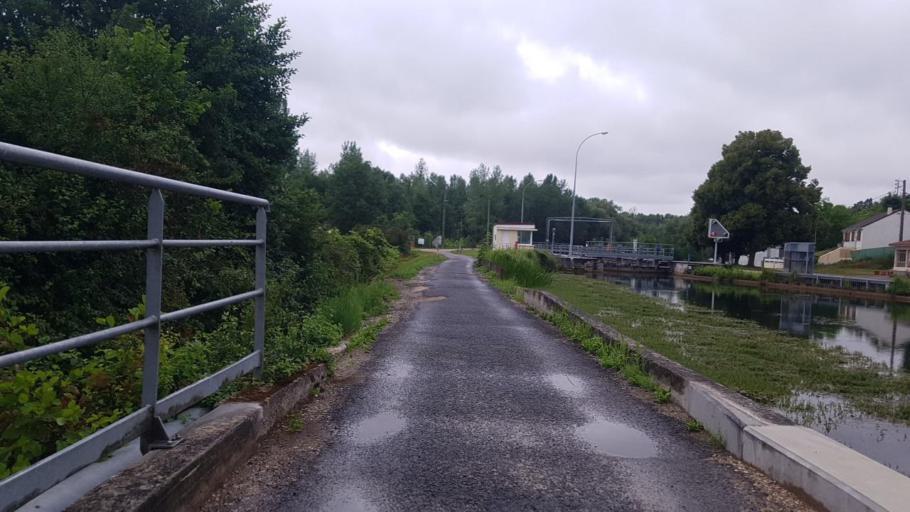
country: FR
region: Champagne-Ardenne
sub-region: Departement de la Marne
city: Vitry-le-Francois
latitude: 48.7489
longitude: 4.5728
